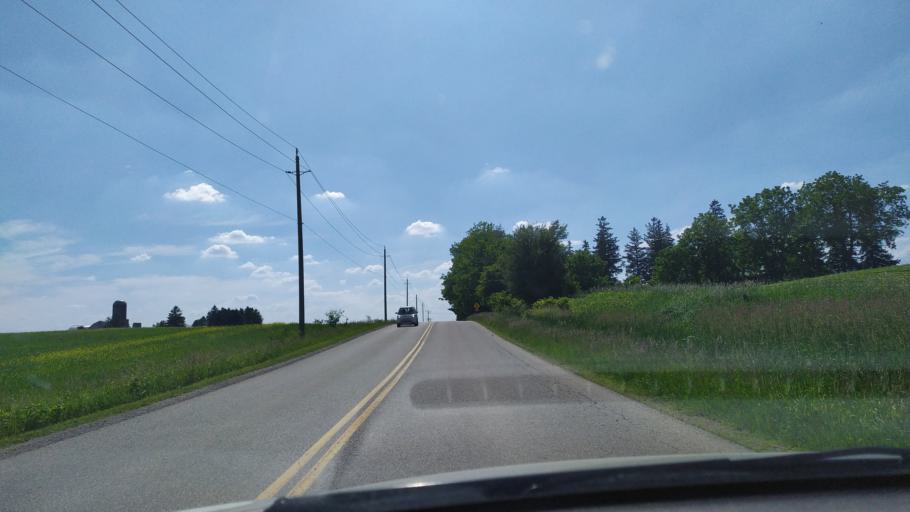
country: CA
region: Ontario
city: Kitchener
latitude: 43.3609
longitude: -80.6265
